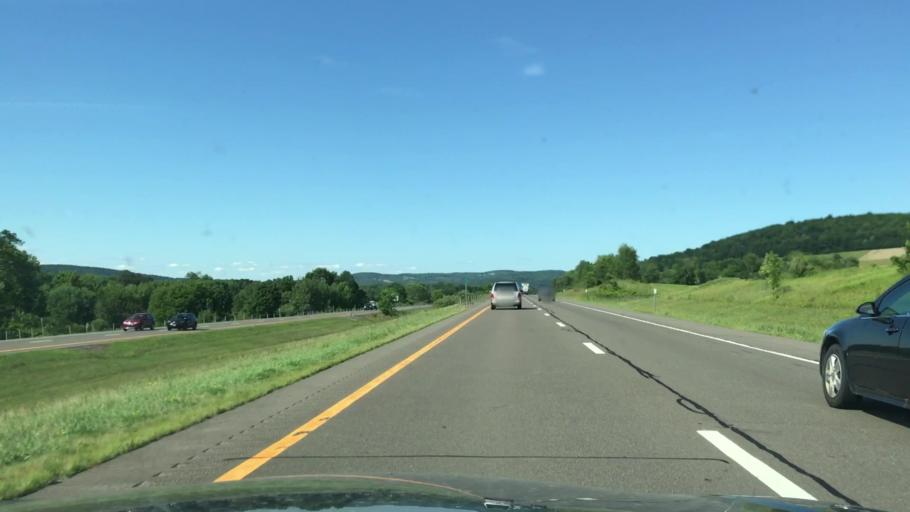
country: US
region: New York
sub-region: Tioga County
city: Owego
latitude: 42.0740
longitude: -76.3133
